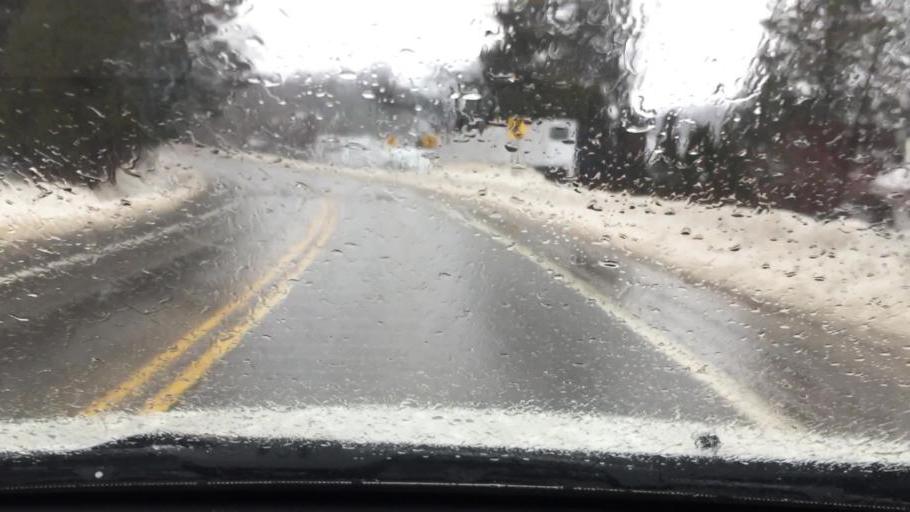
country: US
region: Michigan
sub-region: Charlevoix County
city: Charlevoix
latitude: 45.2484
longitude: -85.1810
